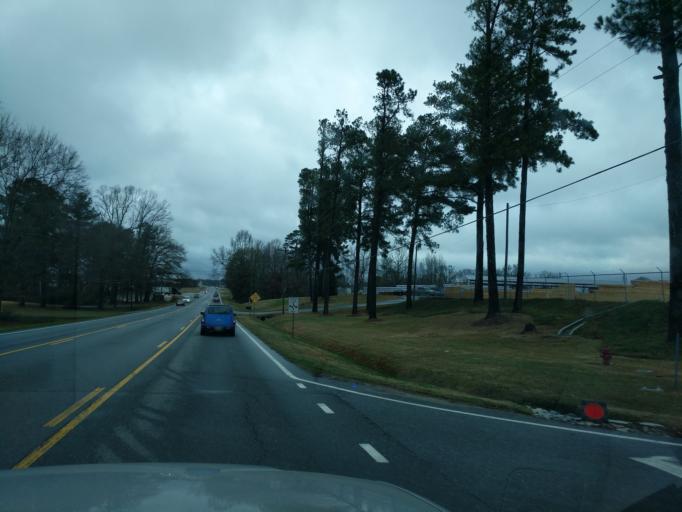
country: US
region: Georgia
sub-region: Franklin County
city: Lavonia
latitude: 34.4183
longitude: -83.1001
